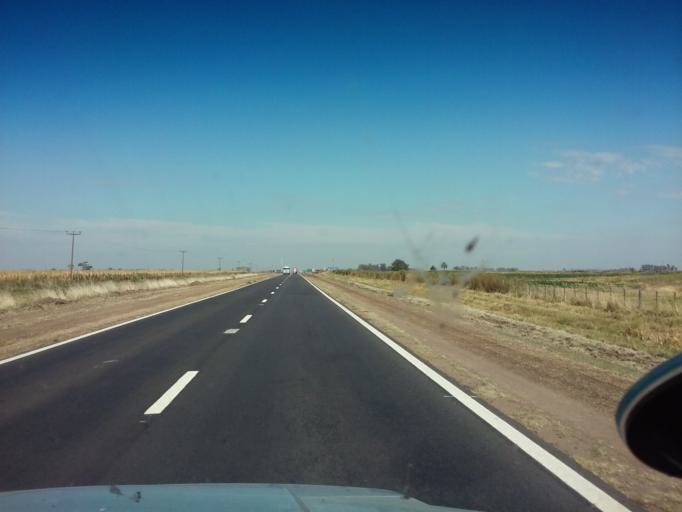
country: AR
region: Buenos Aires
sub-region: Partido de Nueve de Julio
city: Nueve de Julio
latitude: -35.3667
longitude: -60.7101
